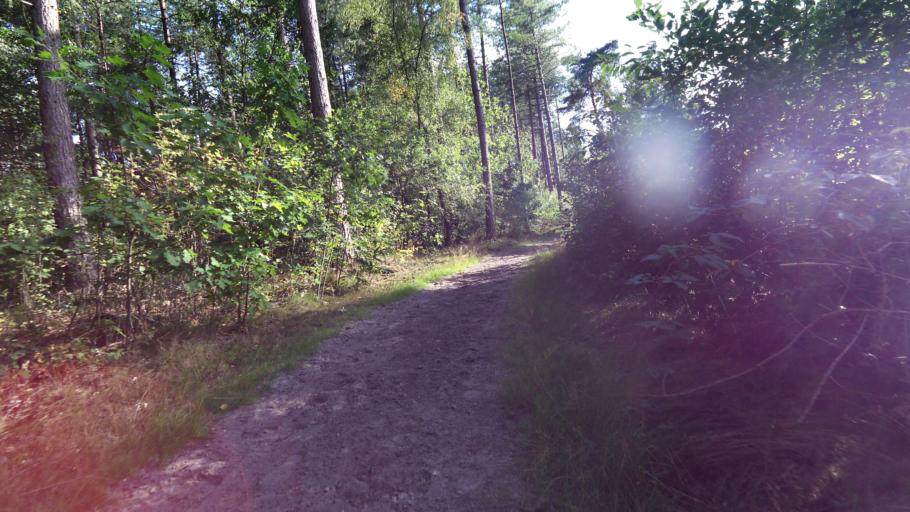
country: NL
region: Gelderland
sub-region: Gemeente Renkum
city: Renkum
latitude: 52.0000
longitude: 5.7219
